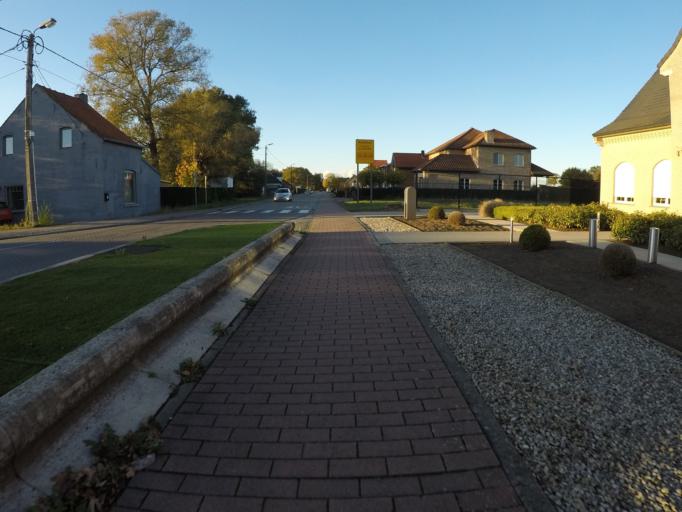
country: BE
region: Flanders
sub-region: Provincie Vlaams-Brabant
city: Begijnendijk
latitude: 51.0287
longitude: 4.7965
